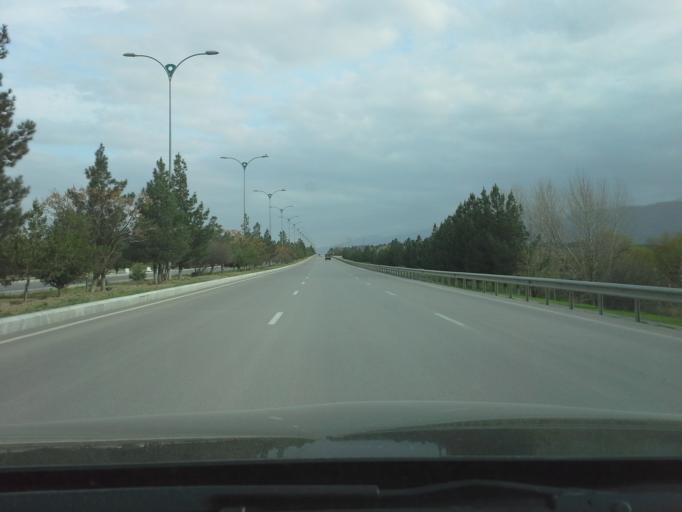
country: TM
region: Ahal
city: Abadan
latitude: 37.9568
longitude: 58.2257
